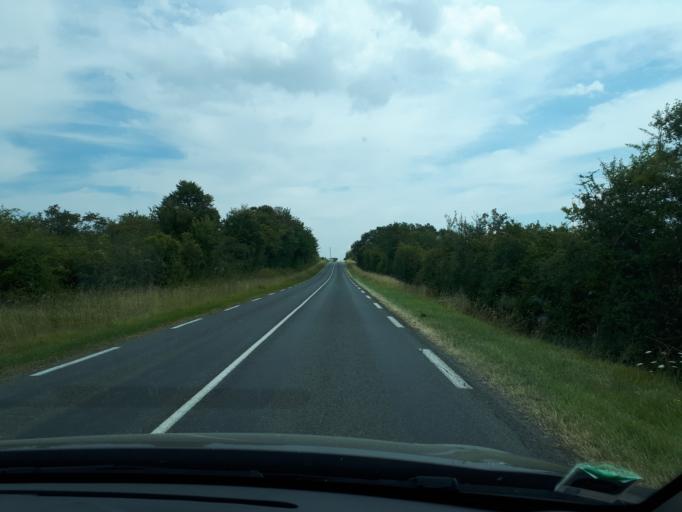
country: FR
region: Centre
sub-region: Departement du Cher
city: Rians
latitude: 47.2382
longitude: 2.6503
